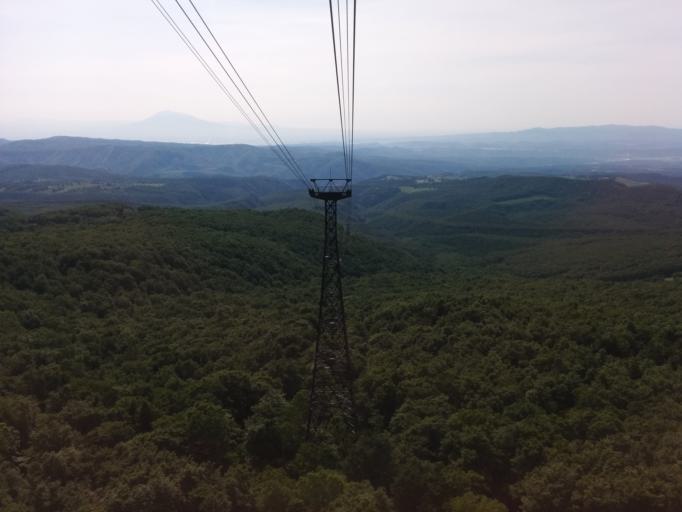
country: JP
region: Aomori
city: Aomori Shi
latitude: 40.6780
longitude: 140.8474
